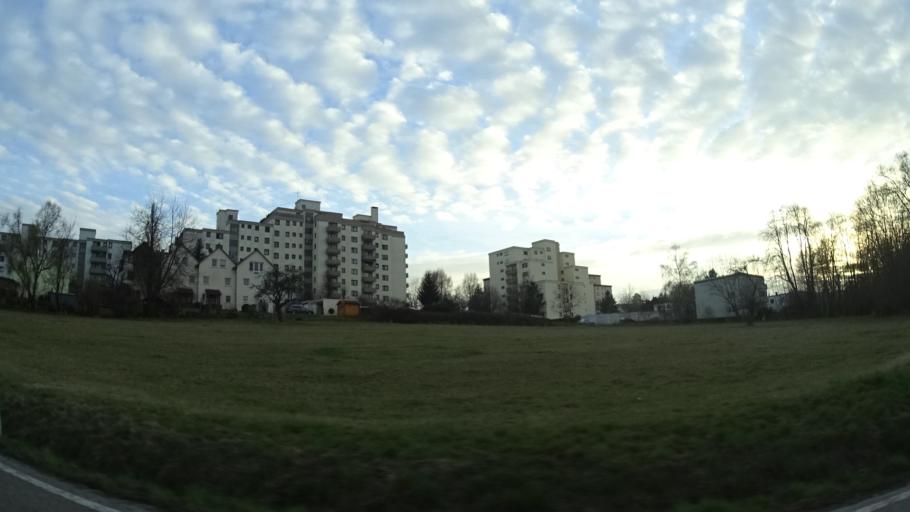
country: DE
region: Baden-Wuerttemberg
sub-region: Regierungsbezirk Stuttgart
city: Hemmingen
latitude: 48.8842
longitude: 9.0062
